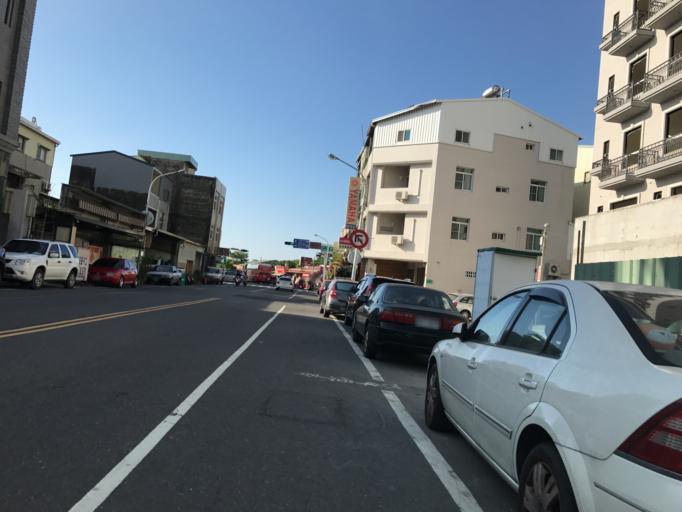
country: TW
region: Taiwan
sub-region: Tainan
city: Tainan
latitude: 23.0017
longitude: 120.1655
